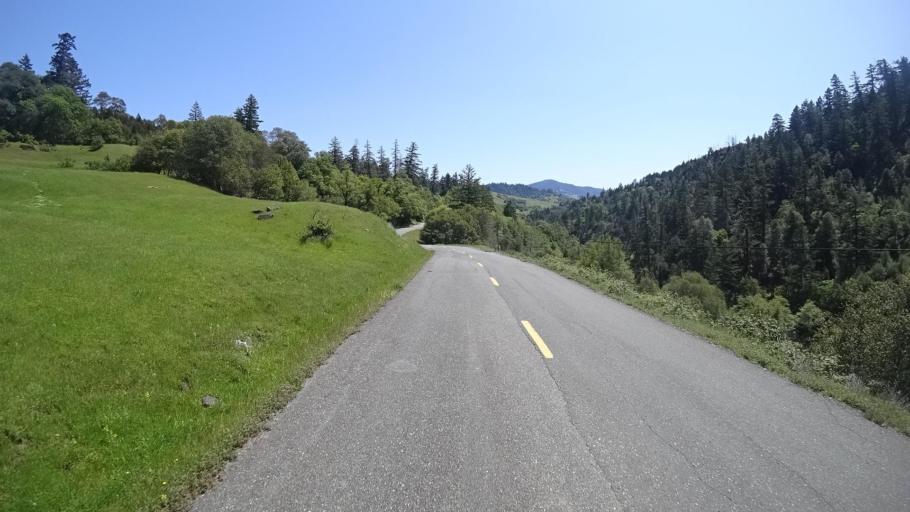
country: US
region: California
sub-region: Humboldt County
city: Redway
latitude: 40.2256
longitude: -123.6074
